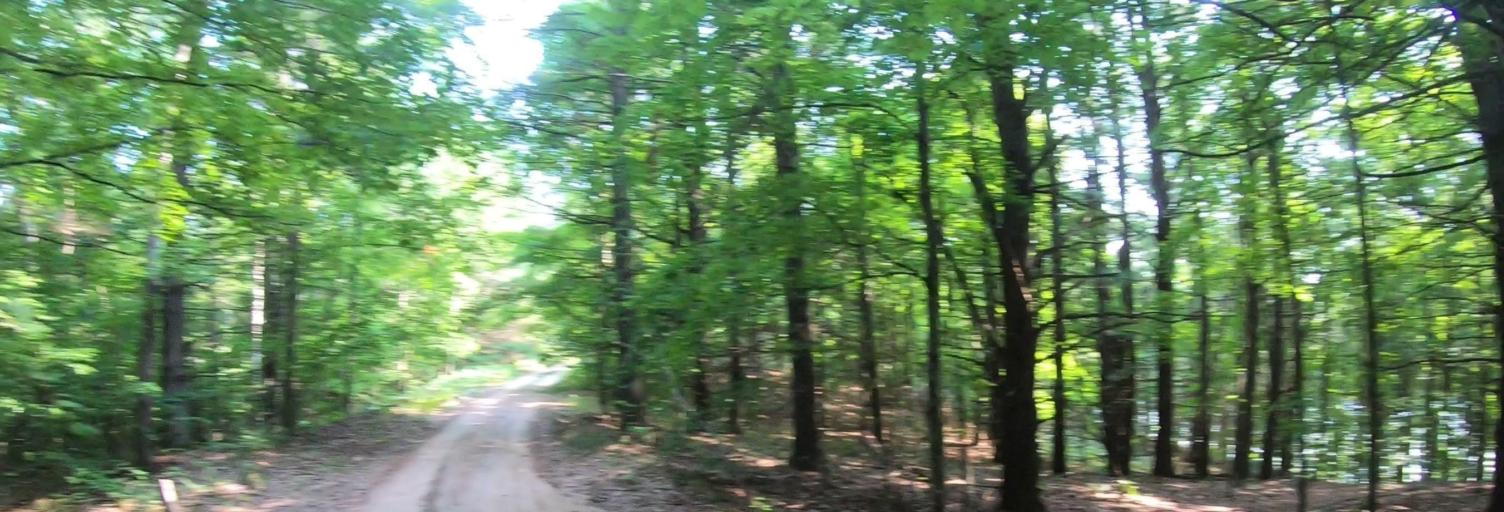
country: US
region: Michigan
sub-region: Benzie County
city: Beulah
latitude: 44.7586
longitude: -85.9265
